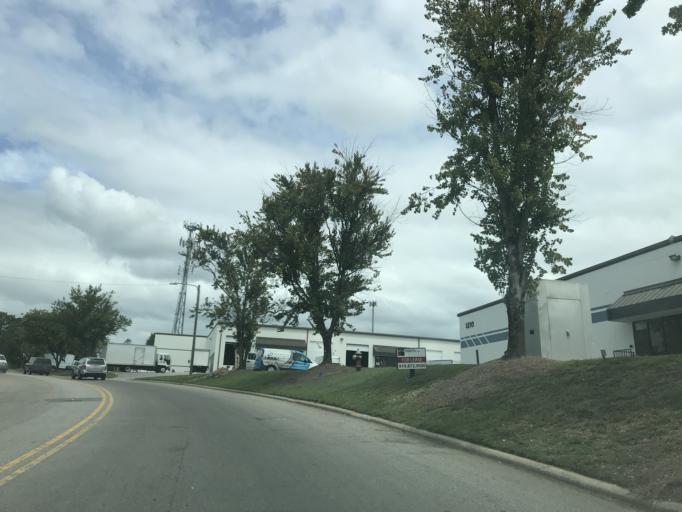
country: US
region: North Carolina
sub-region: Wake County
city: Raleigh
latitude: 35.7952
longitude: -78.5683
